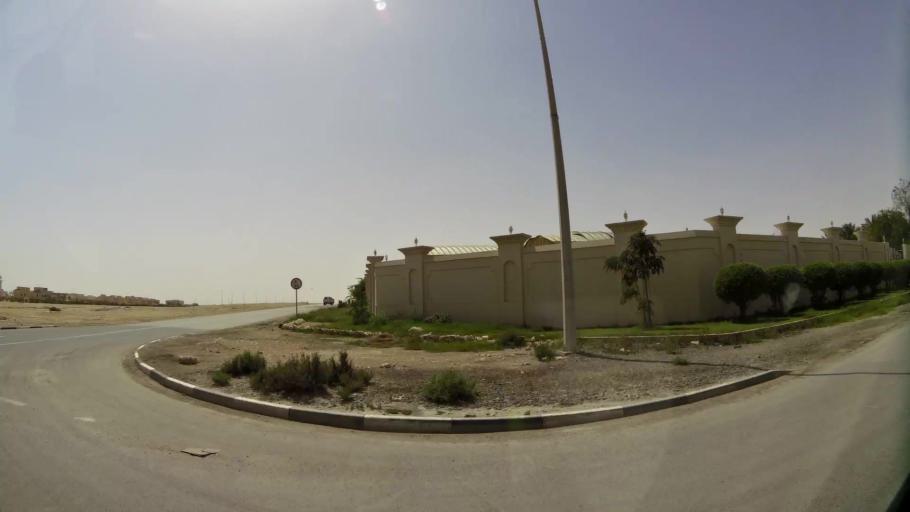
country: QA
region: Baladiyat Umm Salal
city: Umm Salal Muhammad
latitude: 25.3756
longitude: 51.4268
